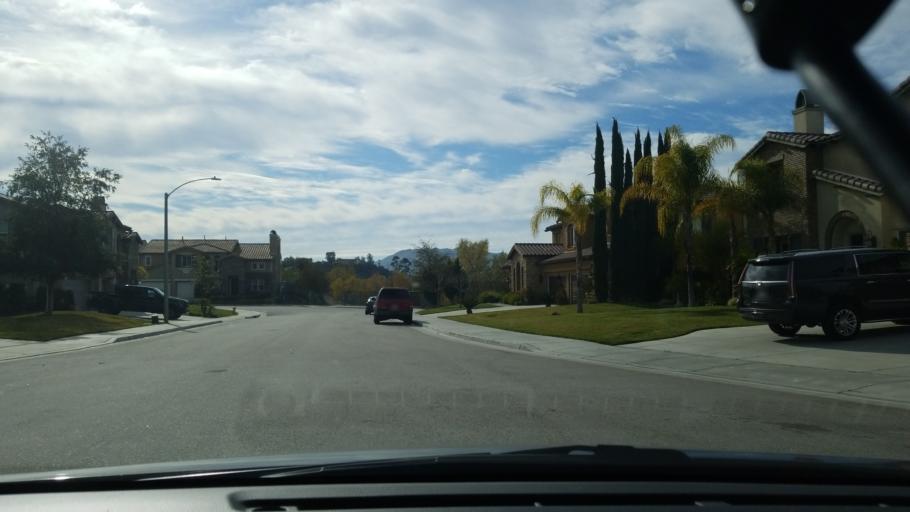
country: US
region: California
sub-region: Riverside County
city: Temecula
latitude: 33.4675
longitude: -117.0672
